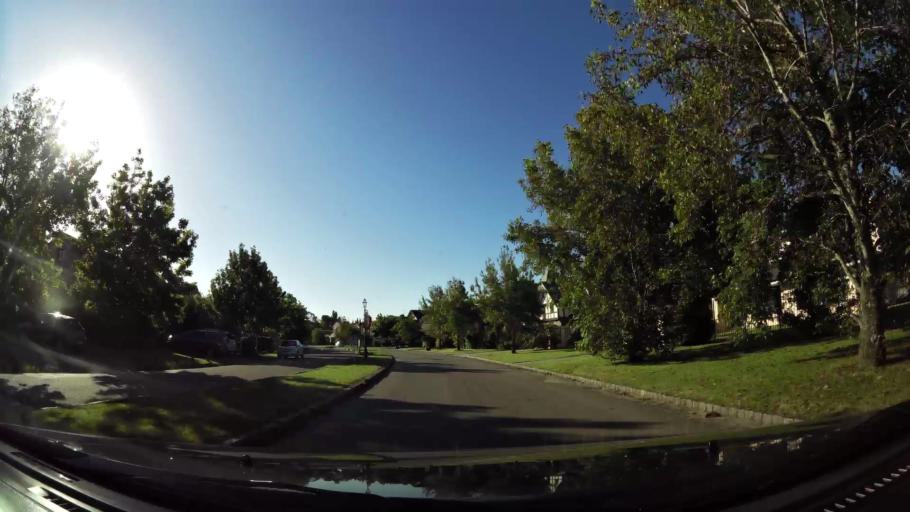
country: UY
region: Canelones
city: Paso de Carrasco
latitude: -34.8705
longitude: -56.0426
